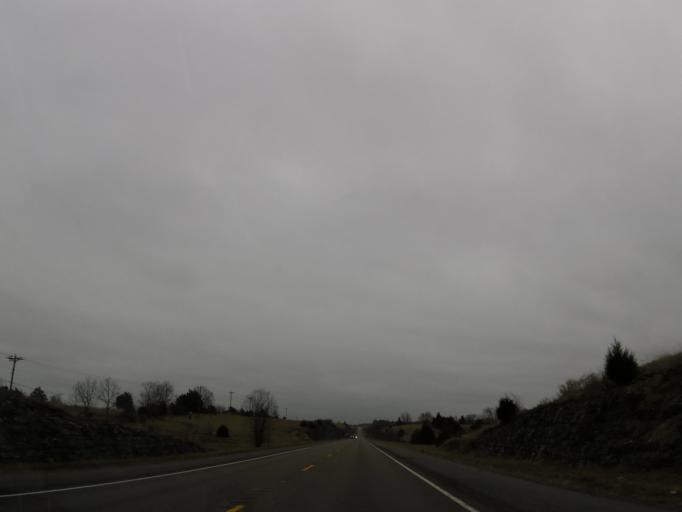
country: US
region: Kentucky
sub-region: Lincoln County
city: Stanford
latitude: 37.5098
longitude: -84.5910
